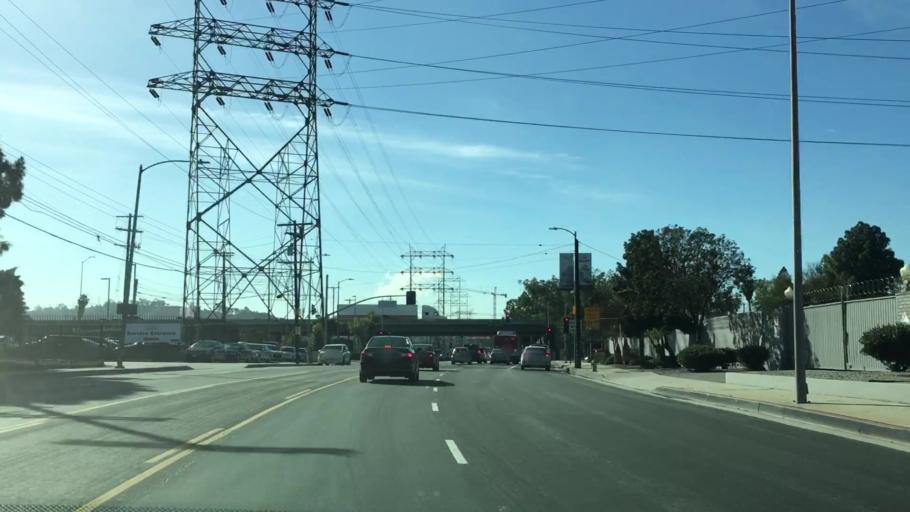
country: US
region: California
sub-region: Los Angeles County
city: Culver City
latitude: 34.0370
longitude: -118.3688
